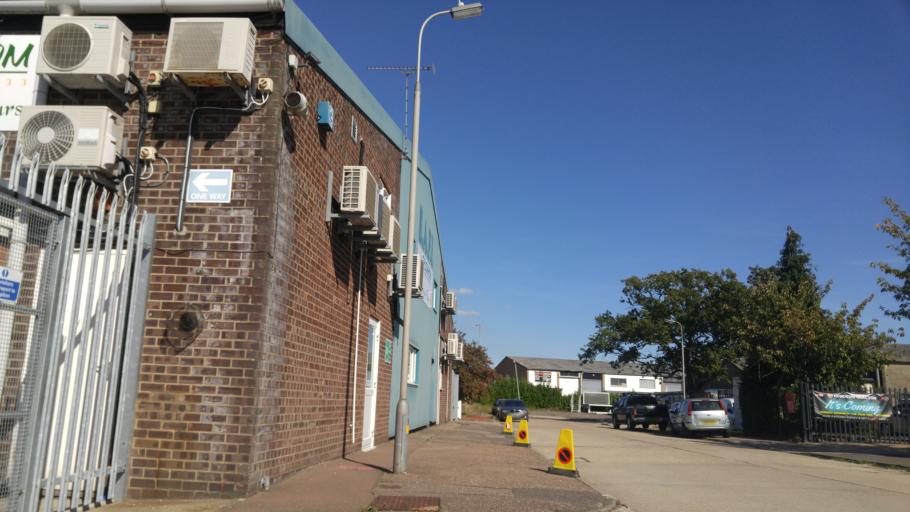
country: GB
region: England
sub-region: Essex
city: Clacton-on-Sea
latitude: 51.8154
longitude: 1.1746
